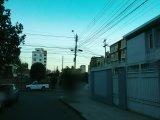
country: BO
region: Cochabamba
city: Cochabamba
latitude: -17.3766
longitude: -66.1577
